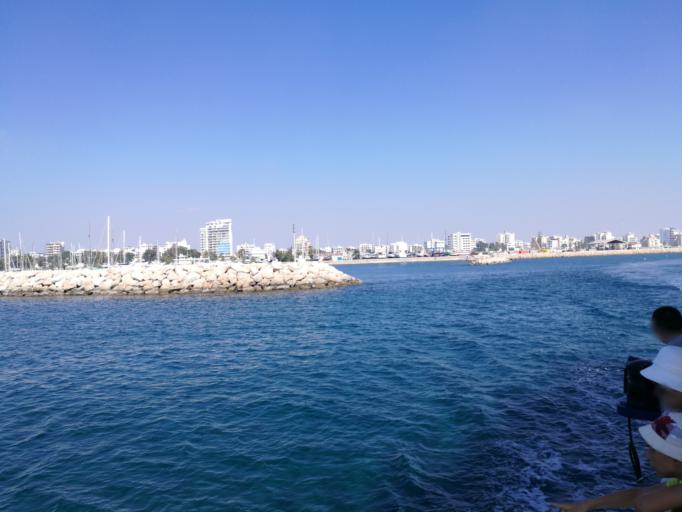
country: CY
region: Larnaka
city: Larnaca
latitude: 34.9181
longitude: 33.6441
